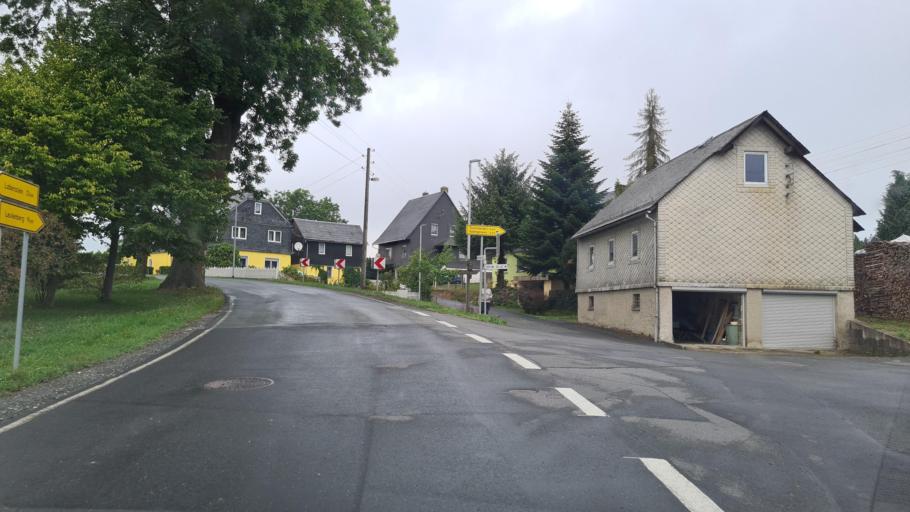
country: DE
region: Thuringia
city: Wurzbach
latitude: 50.5244
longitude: 11.5375
